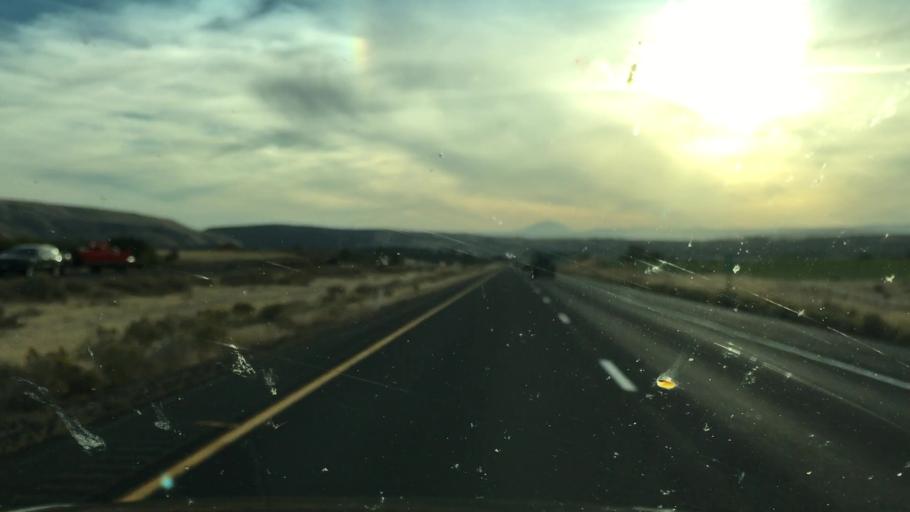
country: US
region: Washington
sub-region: Yakima County
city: Selah
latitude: 46.6831
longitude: -120.4718
